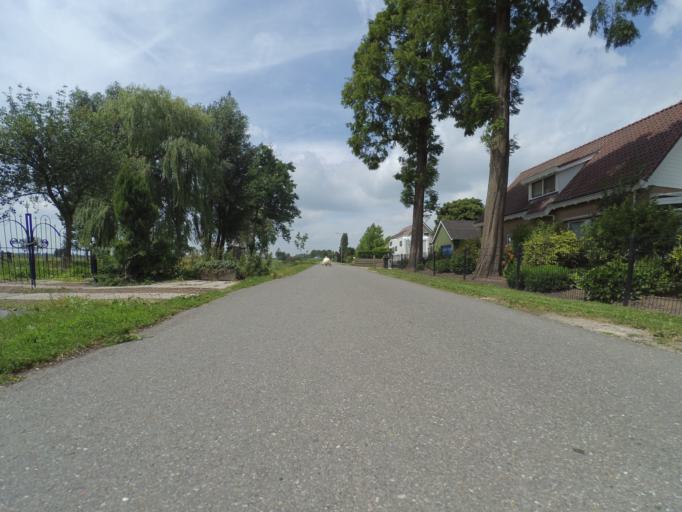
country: NL
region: South Holland
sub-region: Gemeente Leerdam
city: Leerdam
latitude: 51.8701
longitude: 5.0501
